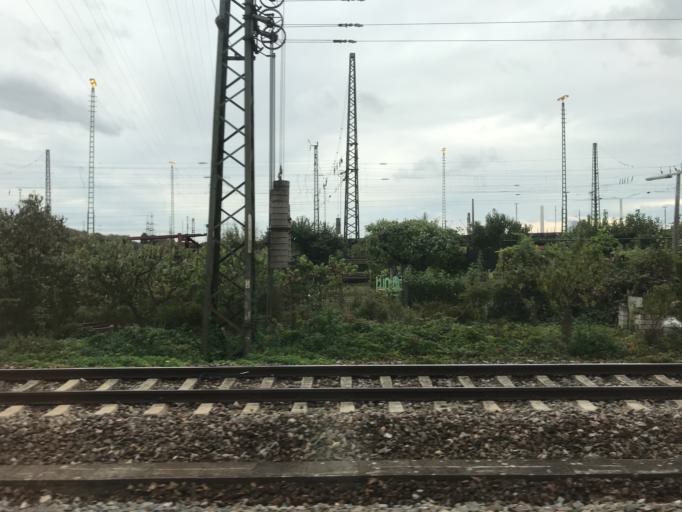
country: DE
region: Baden-Wuerttemberg
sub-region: Karlsruhe Region
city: Ilvesheim
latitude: 49.4537
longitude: 8.5320
